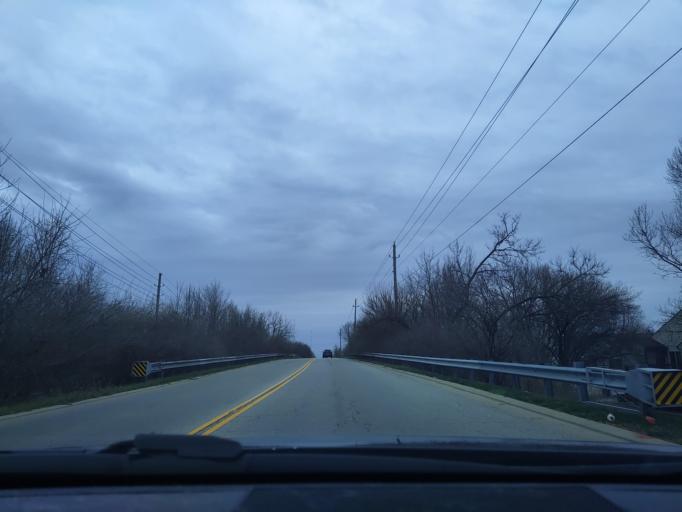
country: US
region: Indiana
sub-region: Marion County
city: Meridian Hills
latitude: 39.9254
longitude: -86.2030
